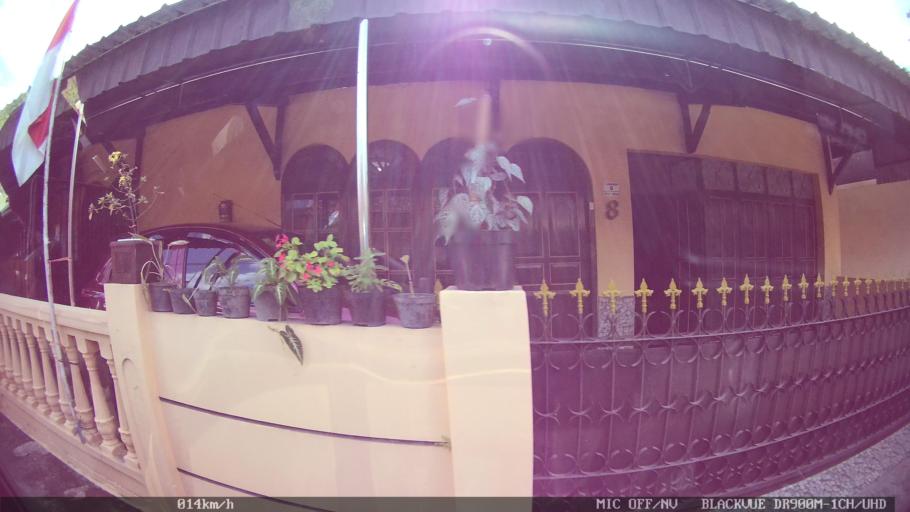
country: ID
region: Daerah Istimewa Yogyakarta
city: Kasihan
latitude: -7.8137
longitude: 110.3553
